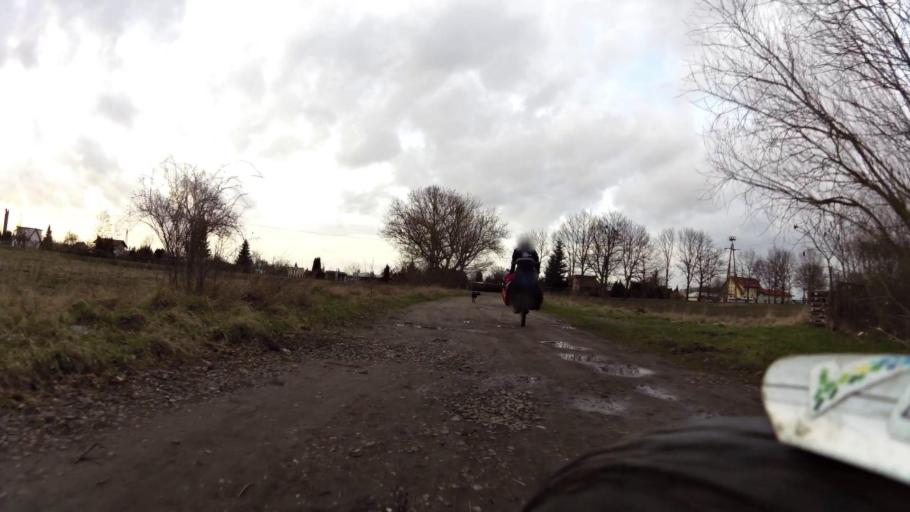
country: PL
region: West Pomeranian Voivodeship
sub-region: Powiat kamienski
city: Kamien Pomorski
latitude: 53.9527
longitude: 14.7722
